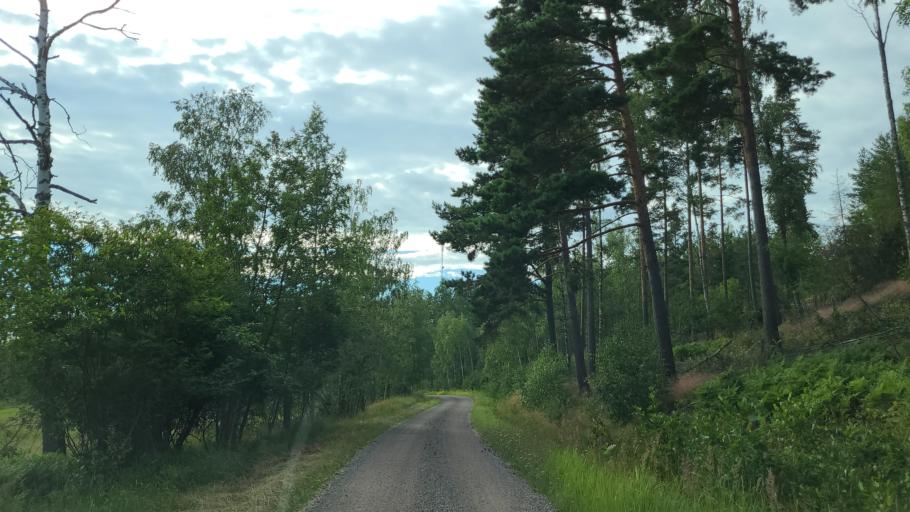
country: FI
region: Varsinais-Suomi
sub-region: Aboland-Turunmaa
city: Nagu
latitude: 60.2827
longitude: 21.9367
